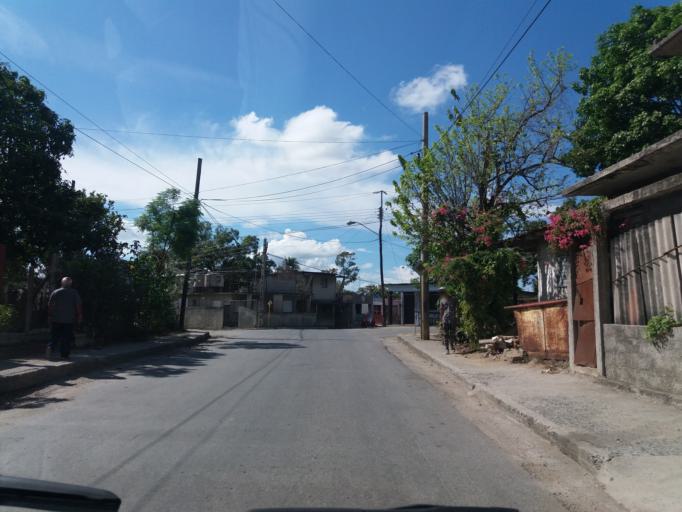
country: CU
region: Cienfuegos
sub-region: Municipio de Cienfuegos
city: Cienfuegos
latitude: 22.1473
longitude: -80.4257
